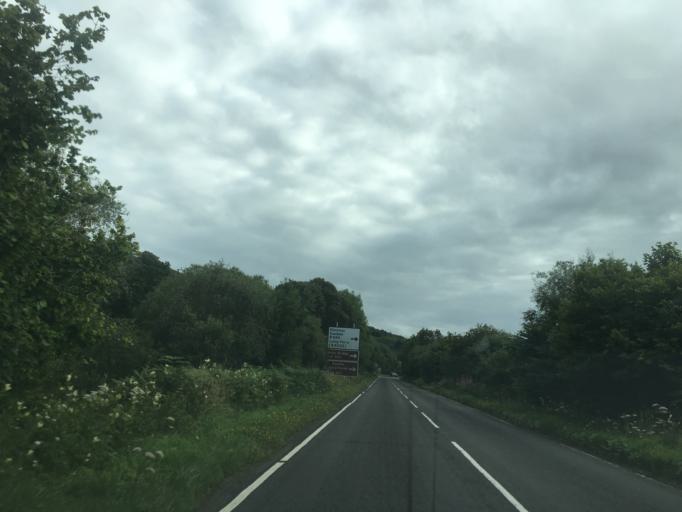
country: GB
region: Scotland
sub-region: Argyll and Bute
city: Oban
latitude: 56.3485
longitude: -5.5039
